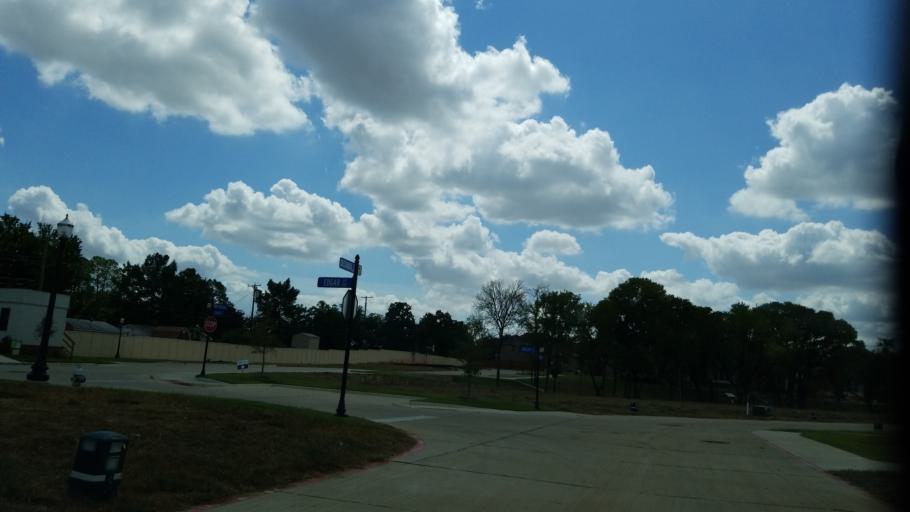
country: US
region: Texas
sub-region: Tarrant County
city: Euless
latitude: 32.8358
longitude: -97.0949
